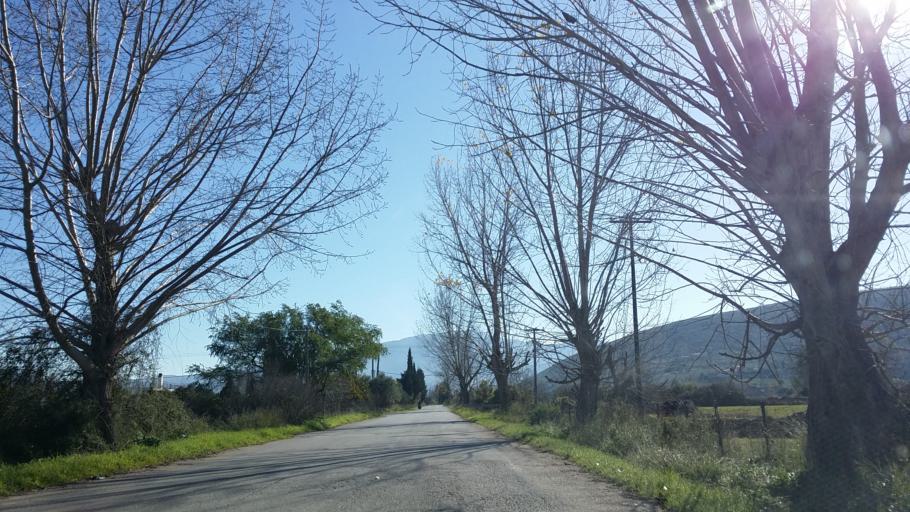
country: GR
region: West Greece
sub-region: Nomos Aitolias kai Akarnanias
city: Vonitsa
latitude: 38.9143
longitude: 20.8821
